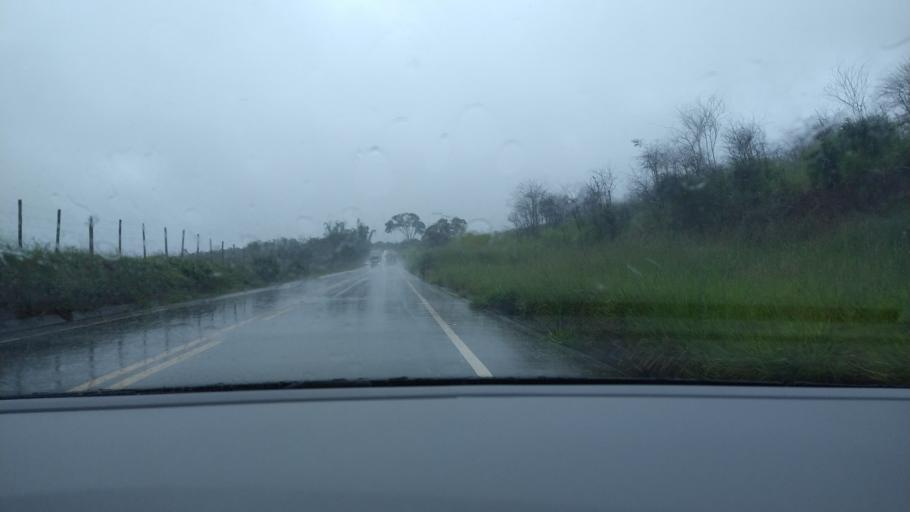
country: BR
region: Minas Gerais
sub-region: Ponte Nova
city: Ponte Nova
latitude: -20.5477
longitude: -42.8855
